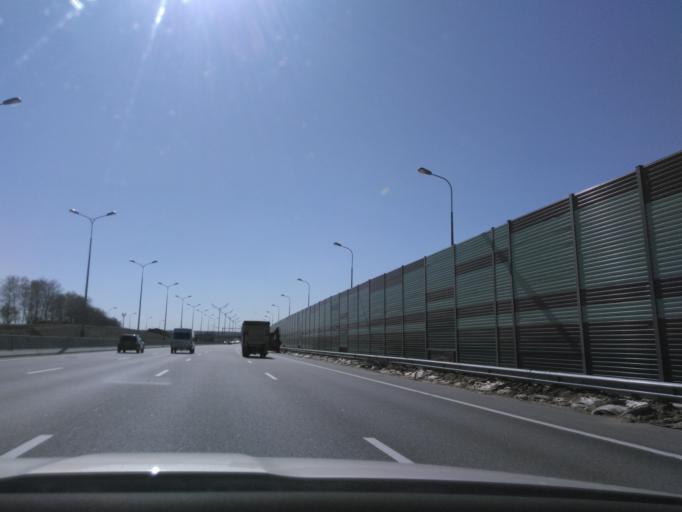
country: RU
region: Moskovskaya
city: Novopodrezkovo
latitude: 55.9650
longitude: 37.3486
